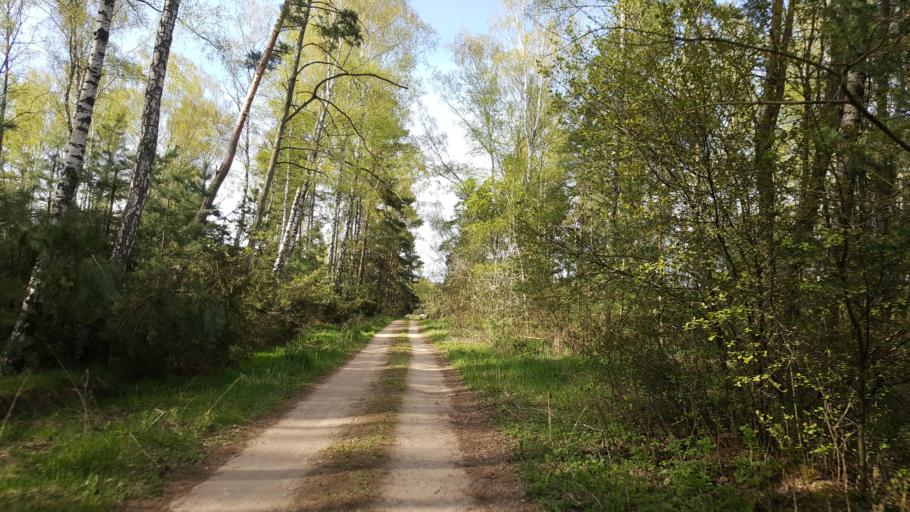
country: BY
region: Brest
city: Vysokaye
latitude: 52.4045
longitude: 23.4719
